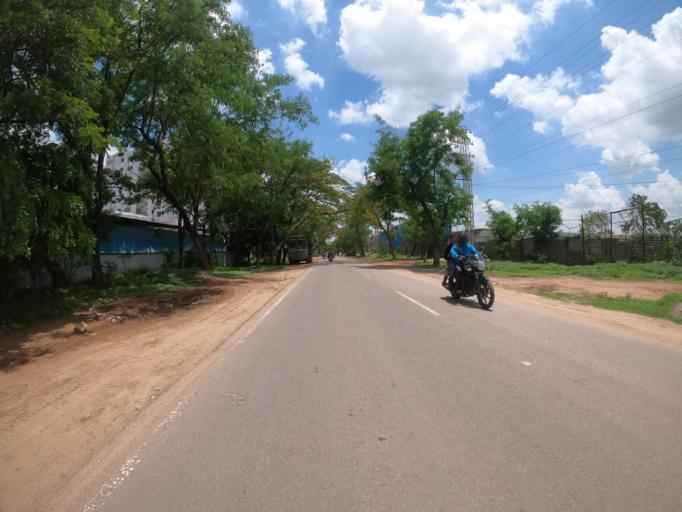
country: IN
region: Telangana
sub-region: Medak
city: Serilingampalle
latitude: 17.3849
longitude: 78.3294
